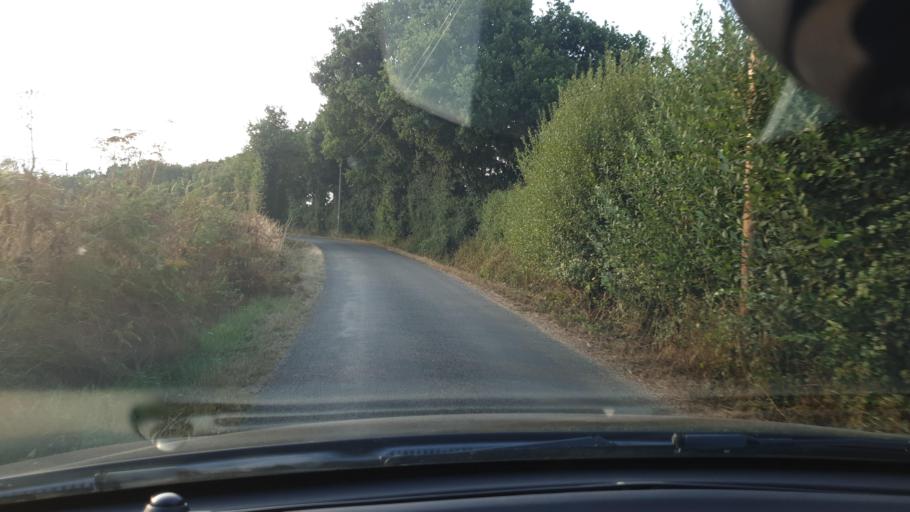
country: GB
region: England
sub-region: Essex
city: Alresford
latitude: 51.9071
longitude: 1.0184
